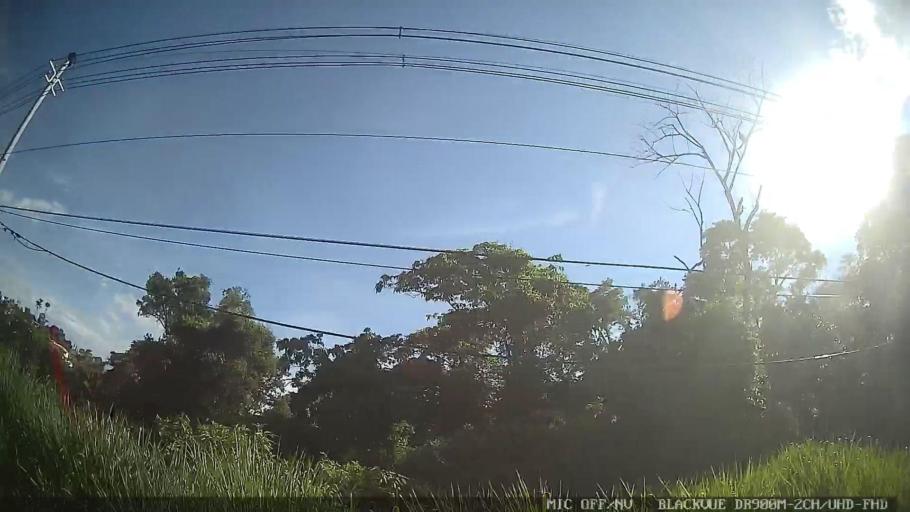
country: BR
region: Sao Paulo
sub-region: Serra Negra
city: Serra Negra
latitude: -22.6103
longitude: -46.7119
